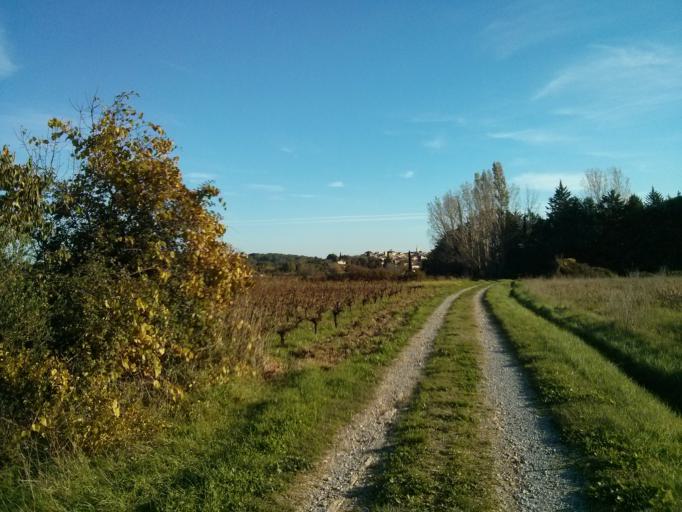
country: FR
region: Languedoc-Roussillon
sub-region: Departement du Gard
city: Aigues-Vives
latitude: 43.7446
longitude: 4.1746
